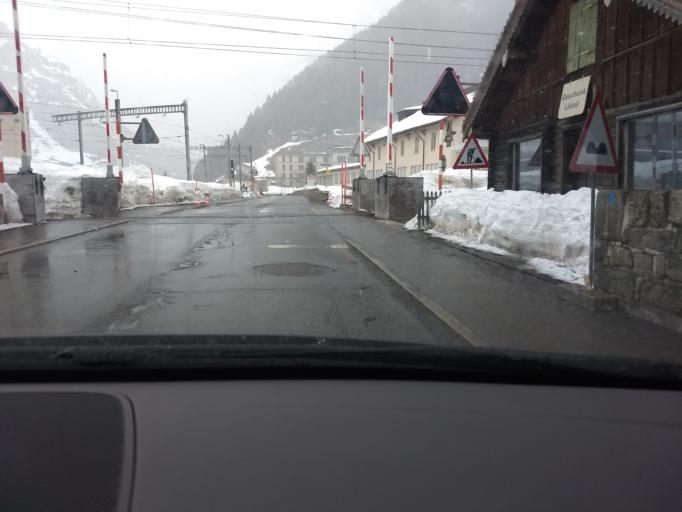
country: CH
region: Uri
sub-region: Uri
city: Andermatt
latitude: 46.6372
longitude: 8.5949
